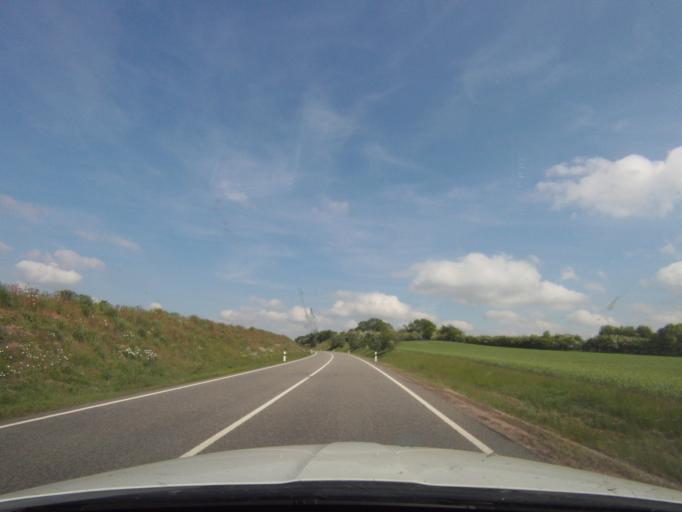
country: DE
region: Thuringia
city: Miesitz
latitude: 50.7363
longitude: 11.8279
